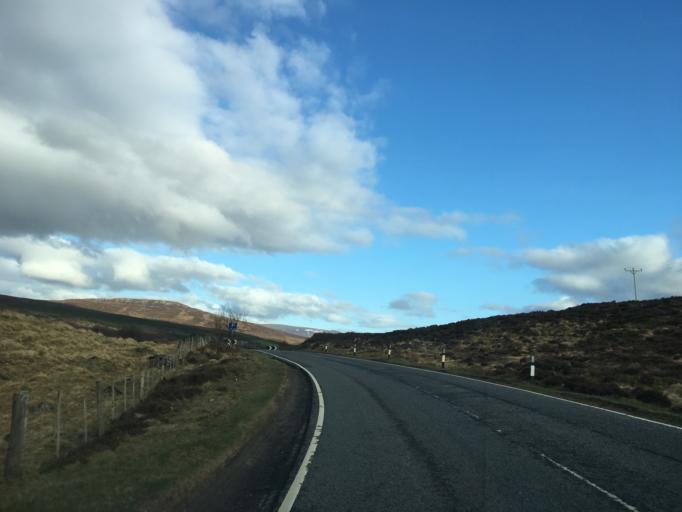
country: GB
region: Scotland
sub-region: Highland
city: Kingussie
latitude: 56.9978
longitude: -4.2503
